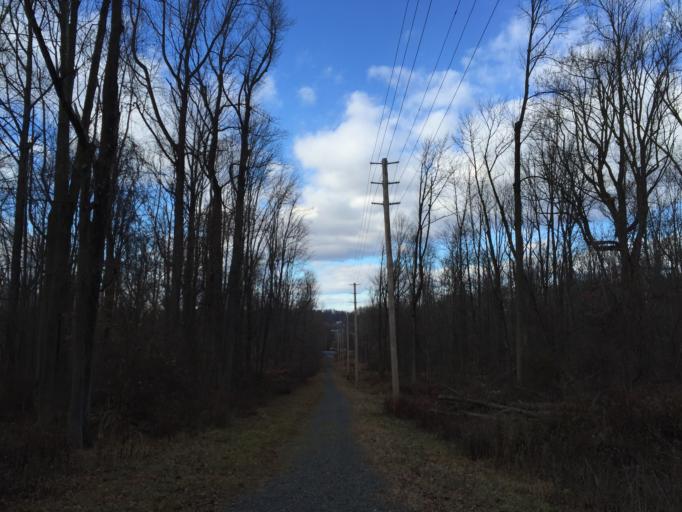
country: US
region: New Jersey
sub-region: Union County
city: New Providence
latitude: 40.6927
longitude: -74.3959
